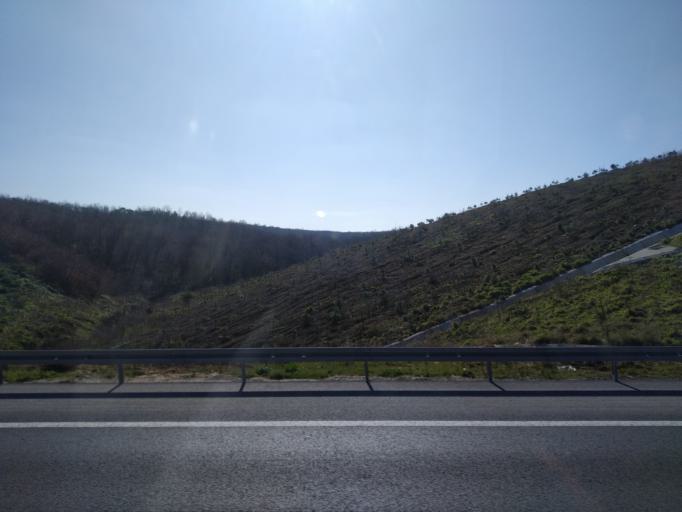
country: TR
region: Istanbul
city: Mahmut Sevket Pasa
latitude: 41.1849
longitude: 29.2210
